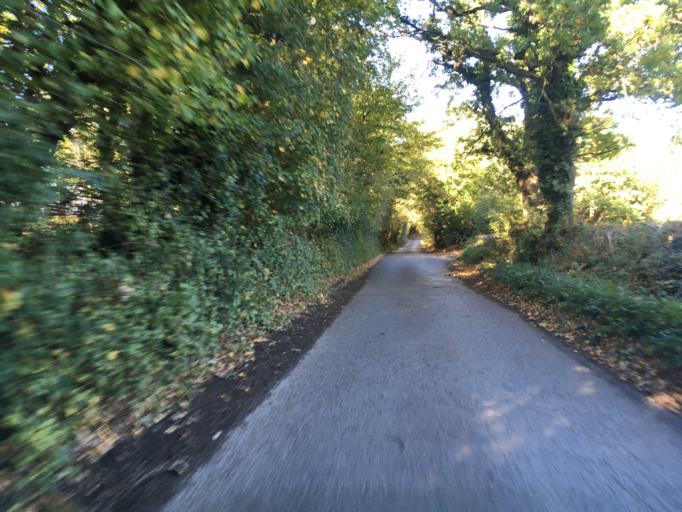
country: GB
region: England
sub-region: South Gloucestershire
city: Yate
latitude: 51.5541
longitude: -2.4281
